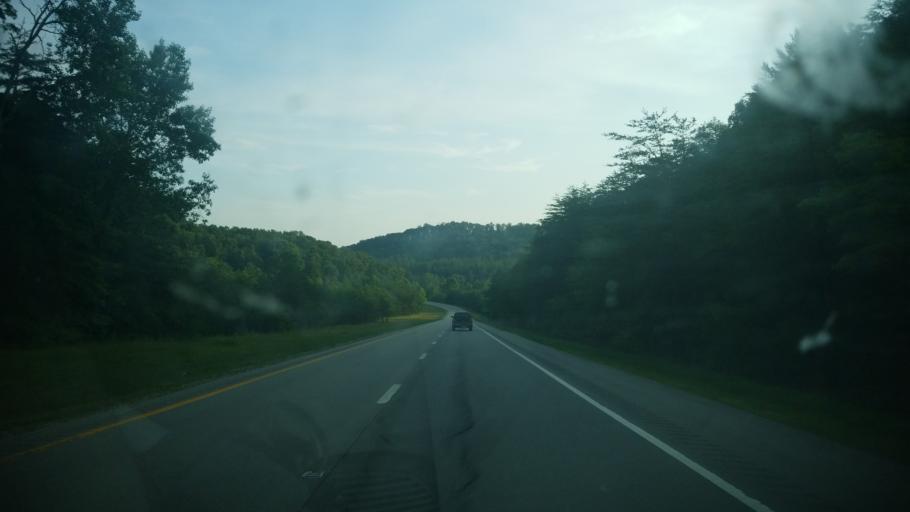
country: US
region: Ohio
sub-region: Adams County
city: Peebles
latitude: 39.0178
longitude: -83.2914
